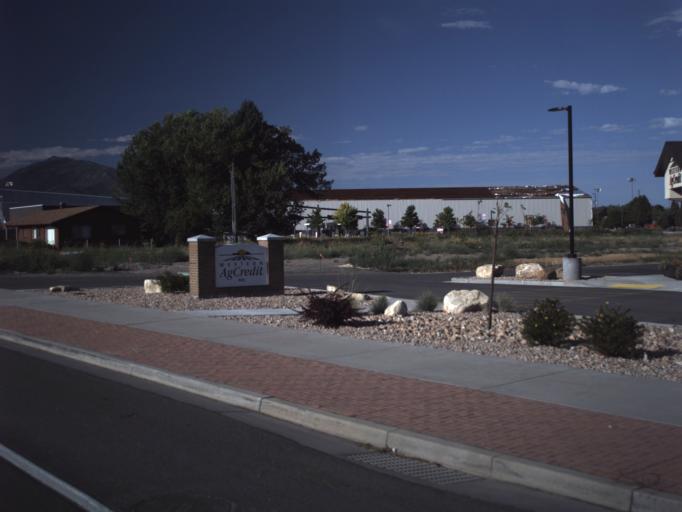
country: US
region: Utah
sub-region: Utah County
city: Spanish Fork
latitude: 40.1009
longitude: -111.6554
